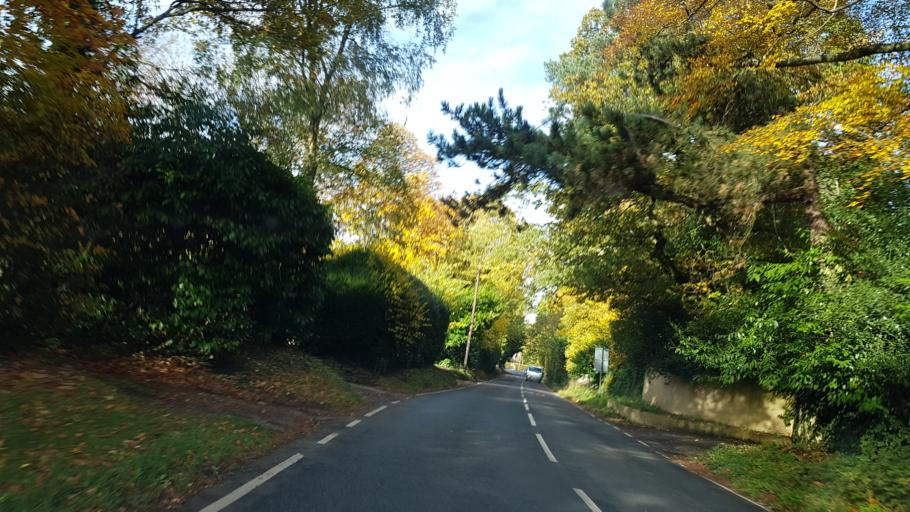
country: GB
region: England
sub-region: Surrey
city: Seale
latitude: 51.2169
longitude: -0.7523
